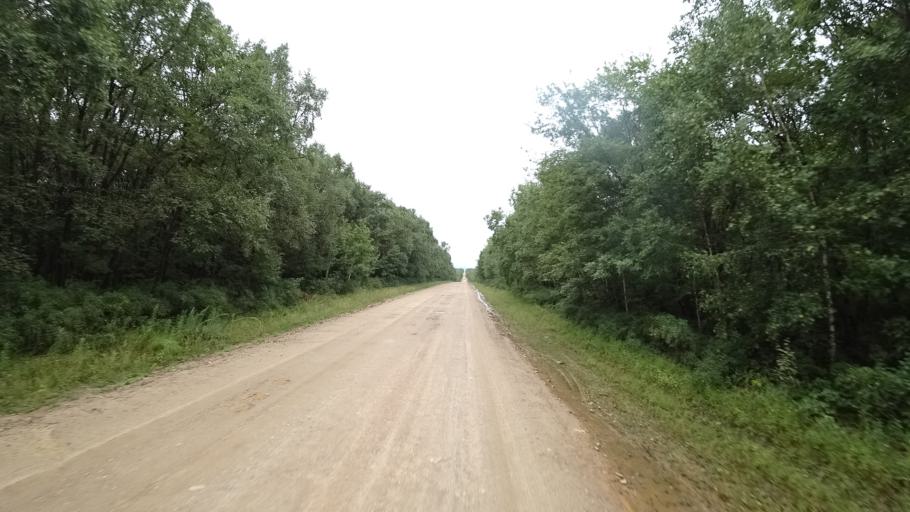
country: RU
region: Primorskiy
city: Ivanovka
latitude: 44.0335
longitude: 132.5323
